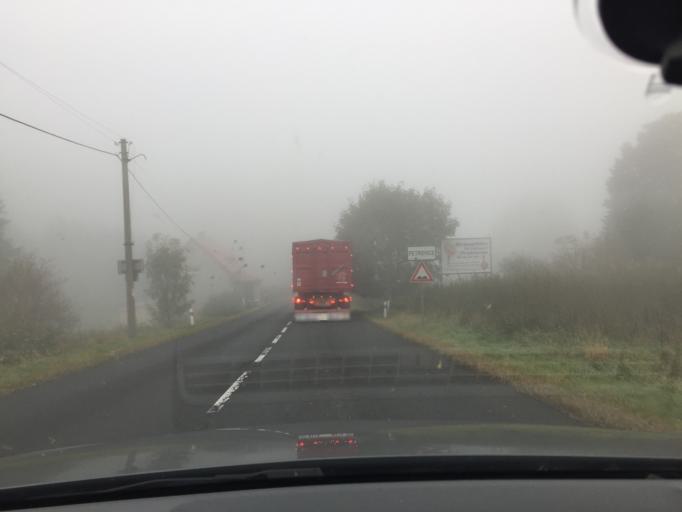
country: CZ
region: Ustecky
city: Libouchec
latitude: 50.7845
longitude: 13.9793
